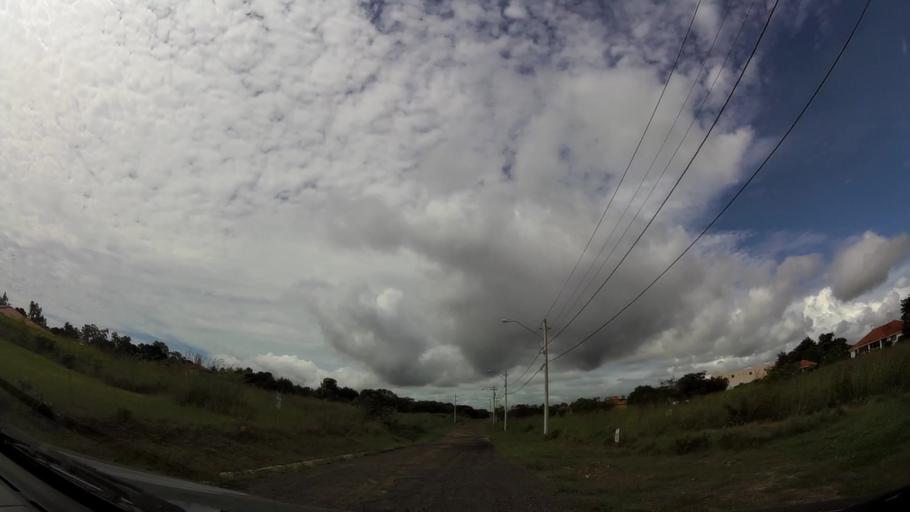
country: PA
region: Panama
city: Nueva Gorgona
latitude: 8.5453
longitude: -79.8897
